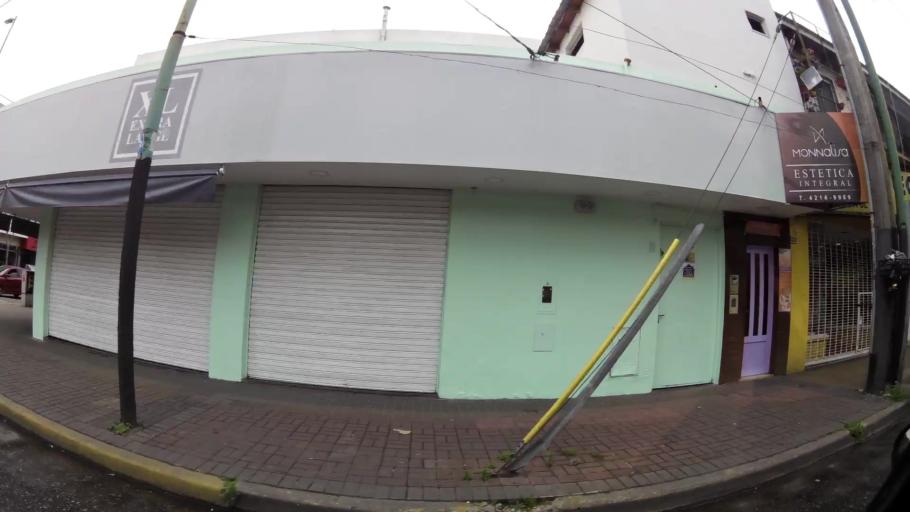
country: AR
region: Buenos Aires
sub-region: Partido de Quilmes
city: Quilmes
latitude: -34.7613
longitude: -58.2080
